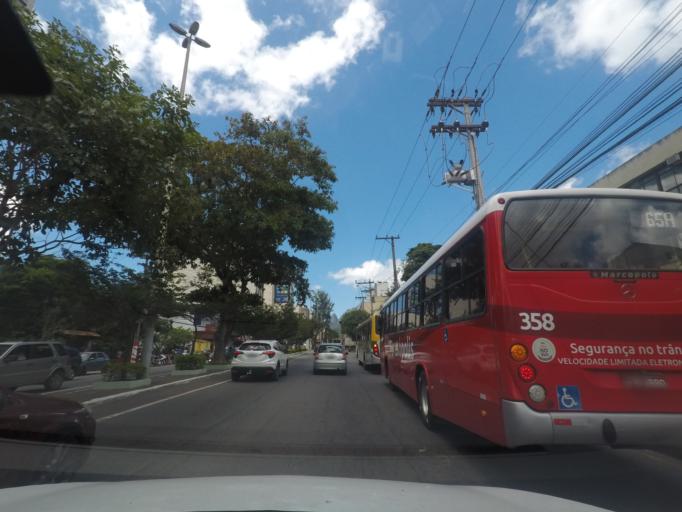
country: BR
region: Rio de Janeiro
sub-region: Teresopolis
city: Teresopolis
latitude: -22.4117
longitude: -42.9688
